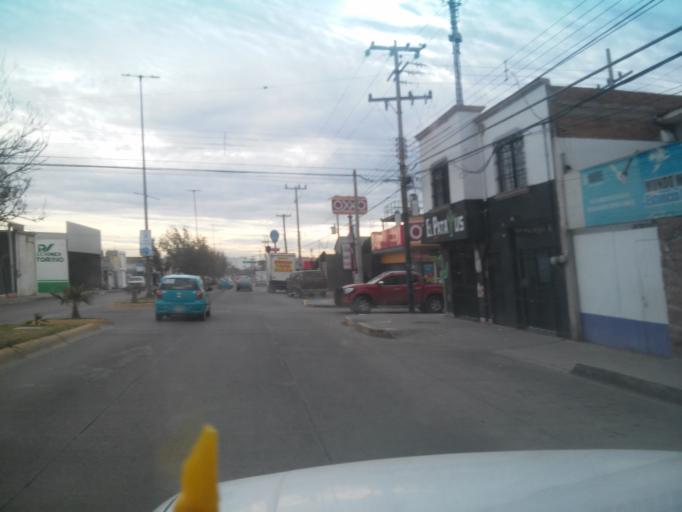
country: MX
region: Durango
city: Victoria de Durango
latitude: 24.0117
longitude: -104.6702
